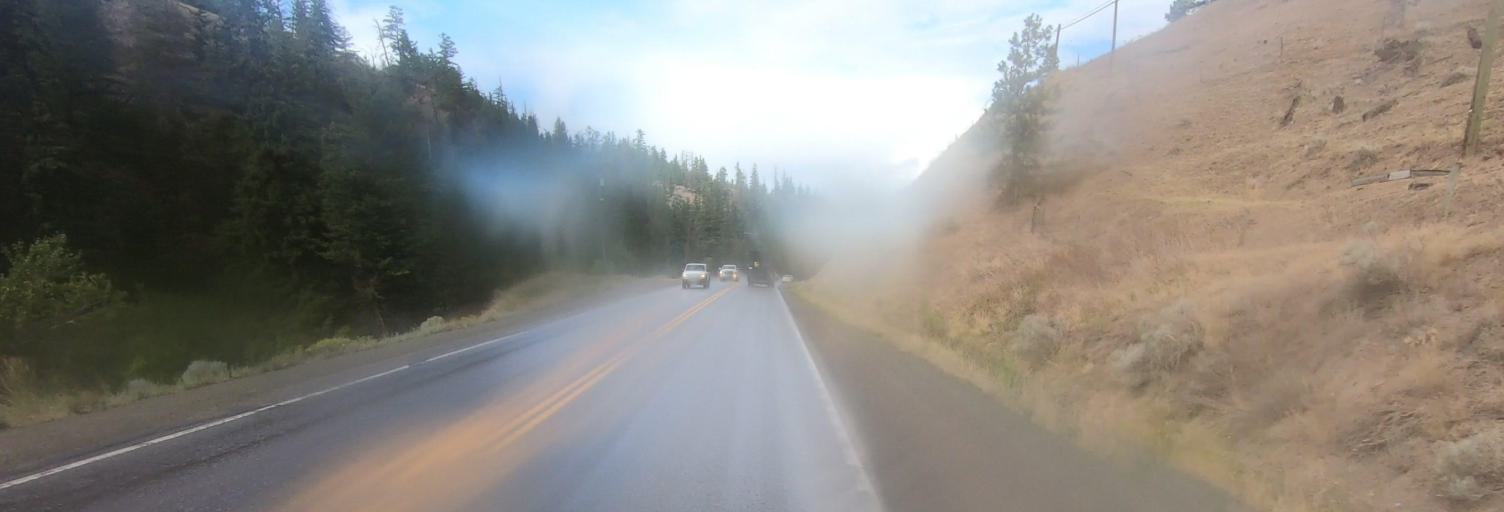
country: CA
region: British Columbia
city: Kamloops
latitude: 50.6712
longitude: -120.5696
